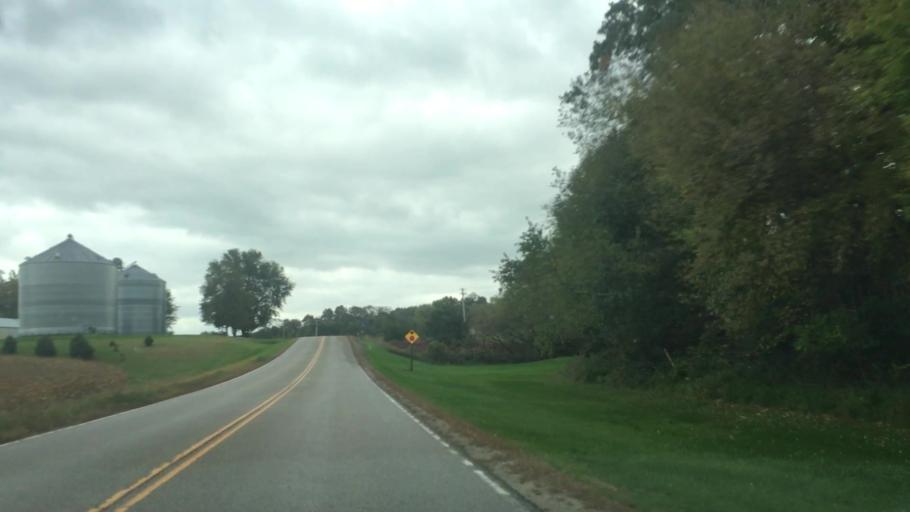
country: US
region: Minnesota
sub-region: Fillmore County
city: Preston
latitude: 43.7357
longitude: -92.0061
